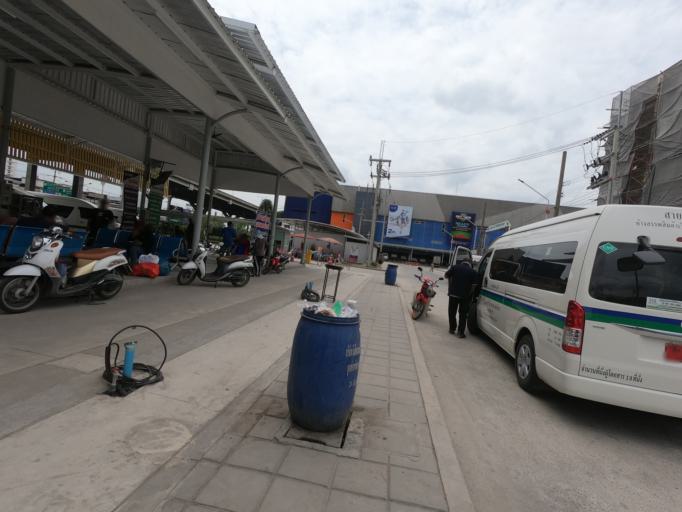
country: TH
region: Bangkok
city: Sai Mai
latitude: 13.9641
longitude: 100.6344
